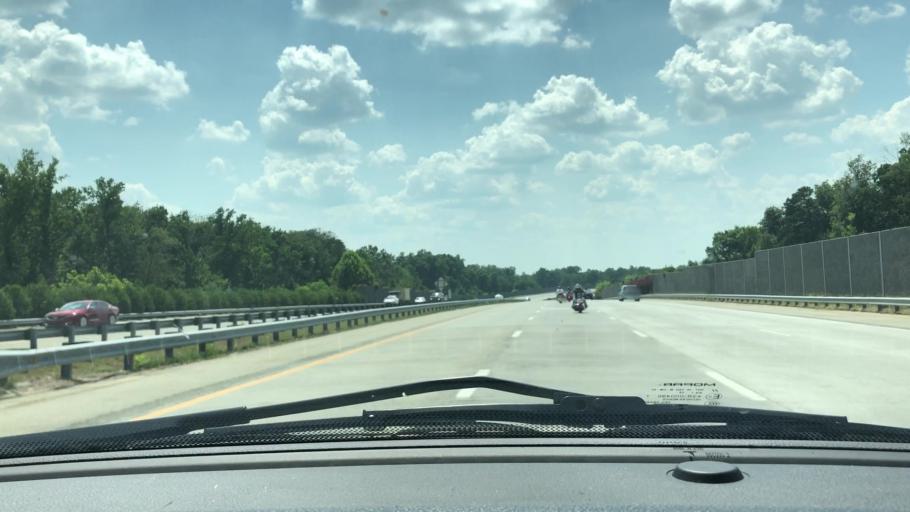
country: US
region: North Carolina
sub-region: Guilford County
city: Jamestown
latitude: 36.0206
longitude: -79.8654
